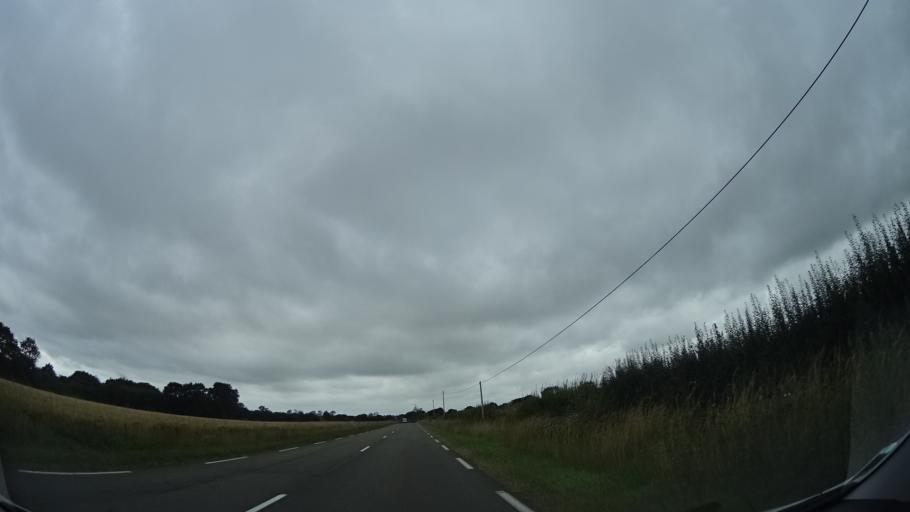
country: FR
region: Lower Normandy
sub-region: Departement de la Manche
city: La Haye-du-Puits
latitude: 49.3132
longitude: -1.6085
